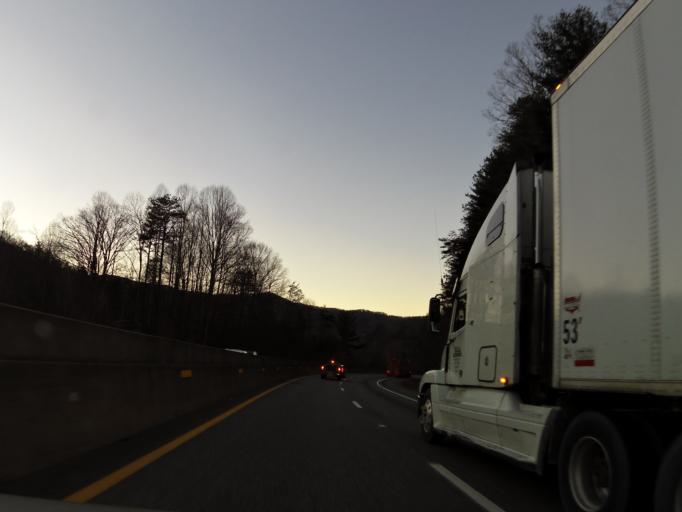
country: US
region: North Carolina
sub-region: Haywood County
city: Cove Creek
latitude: 35.6881
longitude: -83.0322
